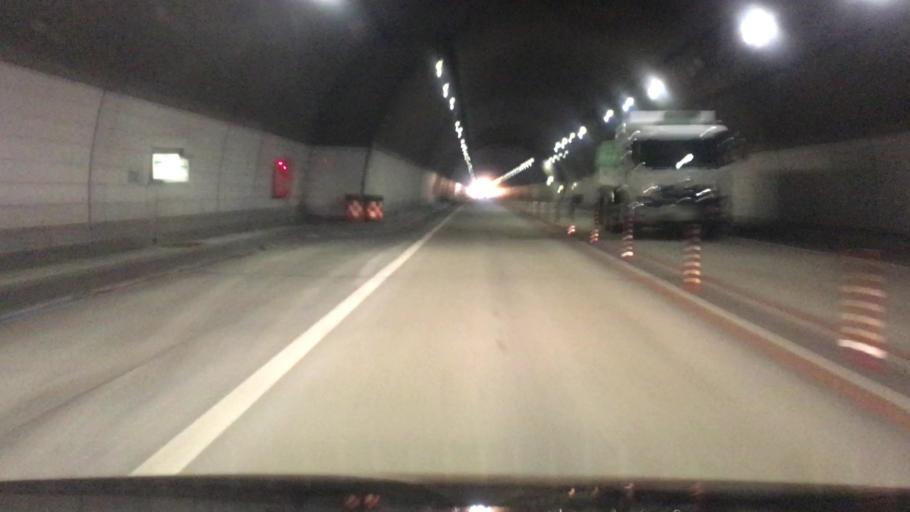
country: JP
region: Kyoto
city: Fukuchiyama
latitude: 35.1643
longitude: 135.0739
